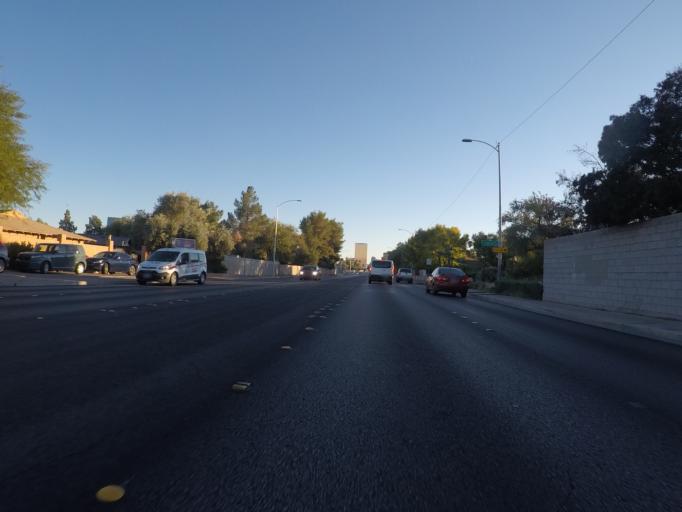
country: US
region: Nevada
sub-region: Clark County
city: Las Vegas
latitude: 36.1540
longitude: -115.1730
